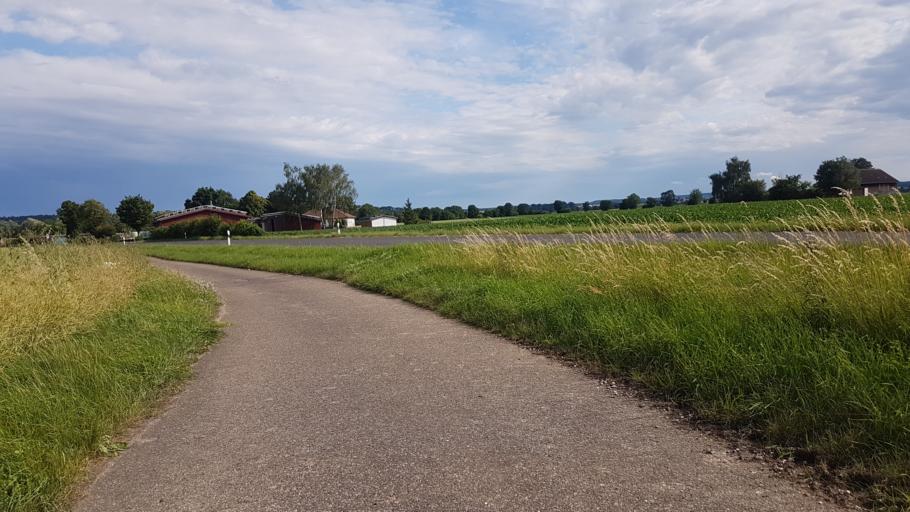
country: DE
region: Baden-Wuerttemberg
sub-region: Tuebingen Region
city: Rottenacker
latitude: 48.2300
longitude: 9.6982
